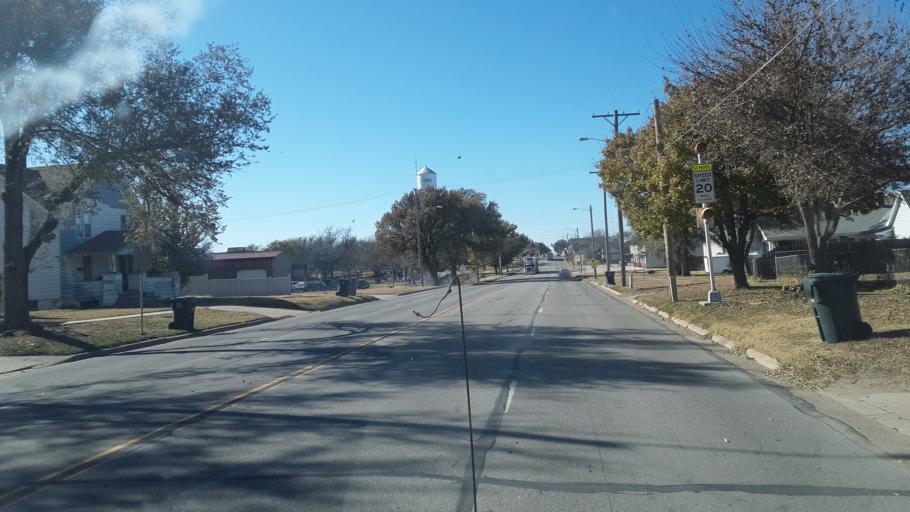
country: US
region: Kansas
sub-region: Rice County
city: Lyons
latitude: 38.3478
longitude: -98.1975
